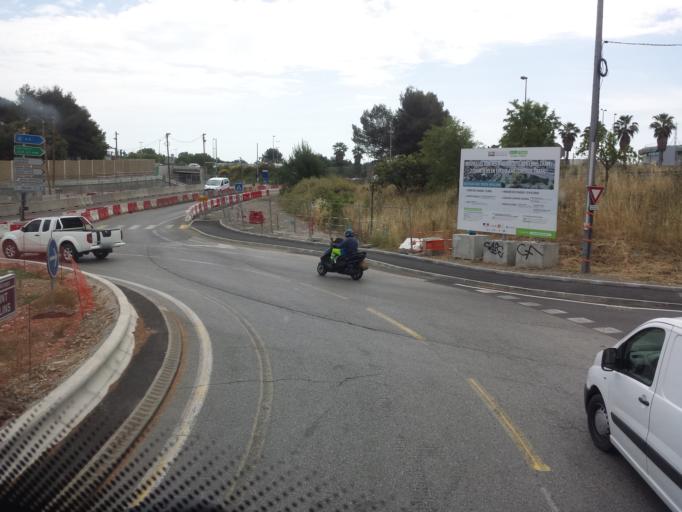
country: FR
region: Provence-Alpes-Cote d'Azur
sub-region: Departement des Alpes-Maritimes
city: Biot
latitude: 43.6043
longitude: 7.0819
